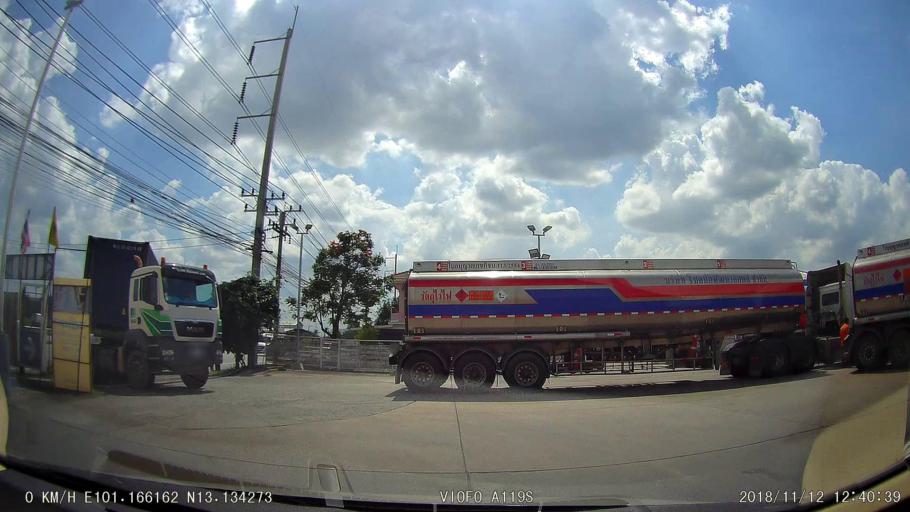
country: TH
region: Rayong
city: Pluak Daeng
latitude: 13.1349
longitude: 101.1665
